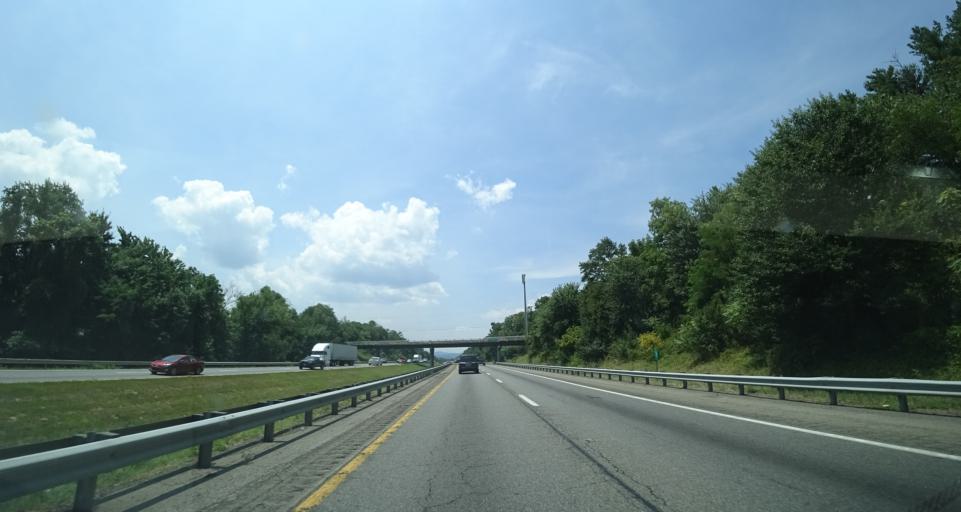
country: US
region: Virginia
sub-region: City of Salem
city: Salem
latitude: 37.3098
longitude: -80.0650
